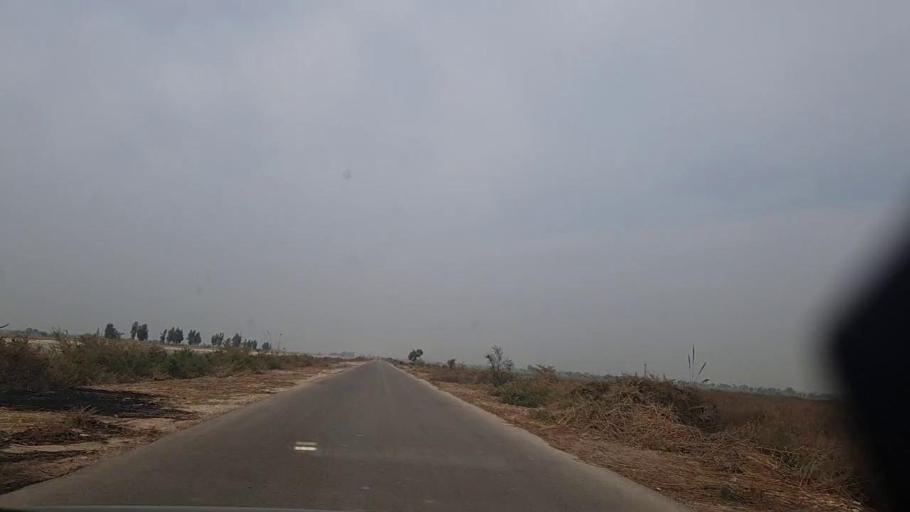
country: PK
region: Sindh
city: Sakrand
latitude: 26.2676
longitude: 68.2376
